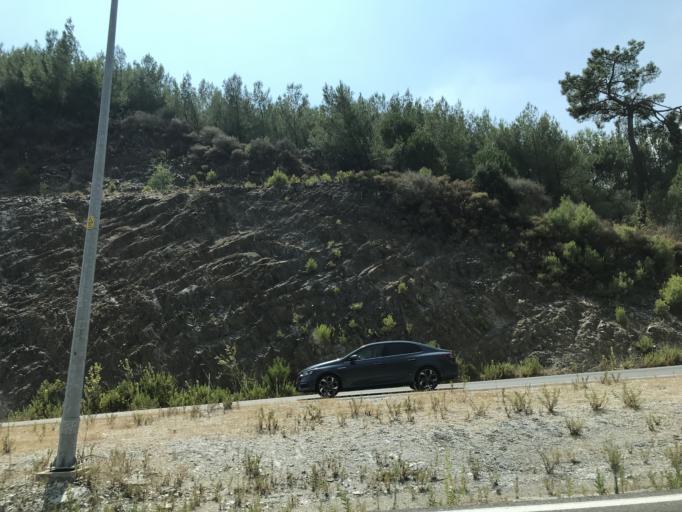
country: TR
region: Mugla
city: Selimiye
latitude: 37.4228
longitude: 27.5677
